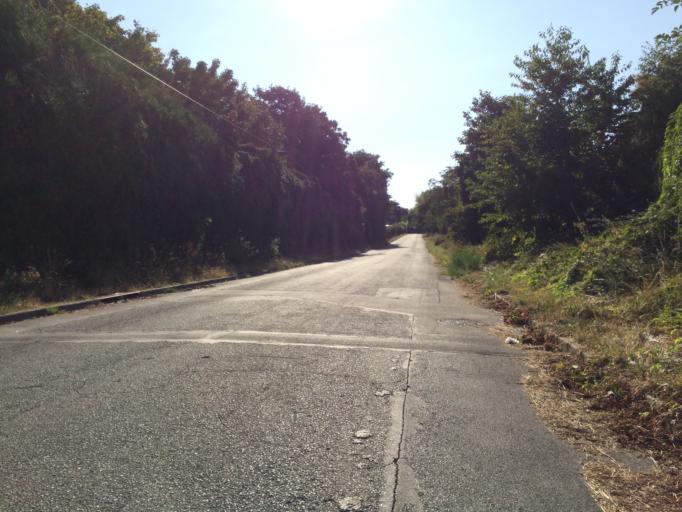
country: FR
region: Ile-de-France
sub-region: Departement de l'Essonne
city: Epinay-sur-Orge
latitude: 48.6662
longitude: 2.3135
